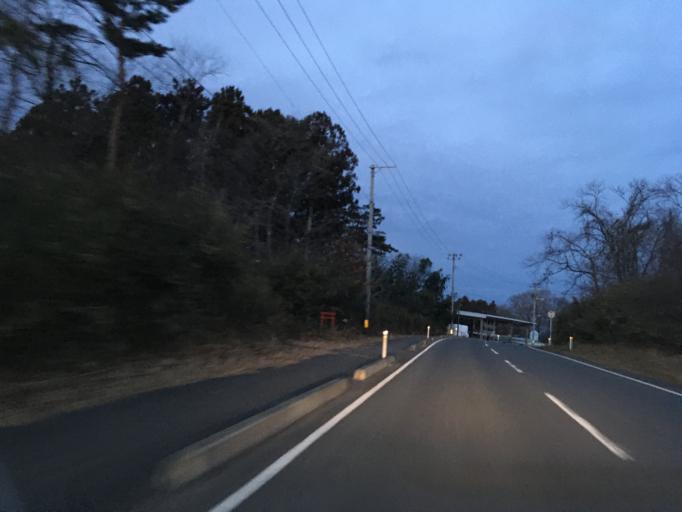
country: JP
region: Miyagi
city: Kogota
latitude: 38.6962
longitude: 141.1009
